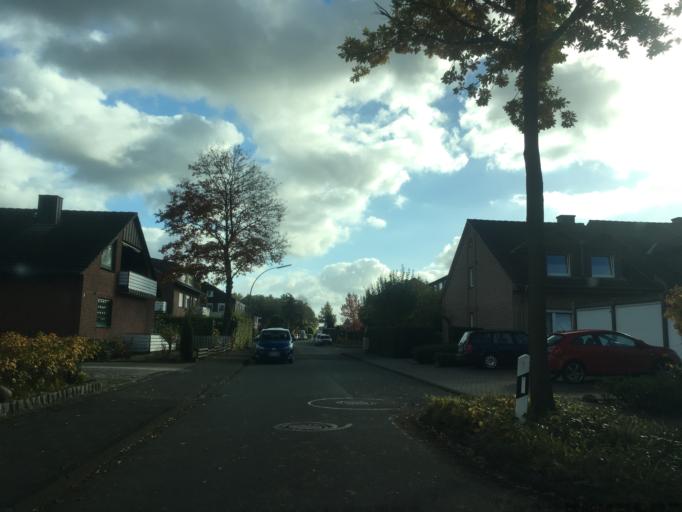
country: DE
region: North Rhine-Westphalia
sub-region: Regierungsbezirk Munster
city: Havixbeck
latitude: 51.9833
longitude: 7.4151
